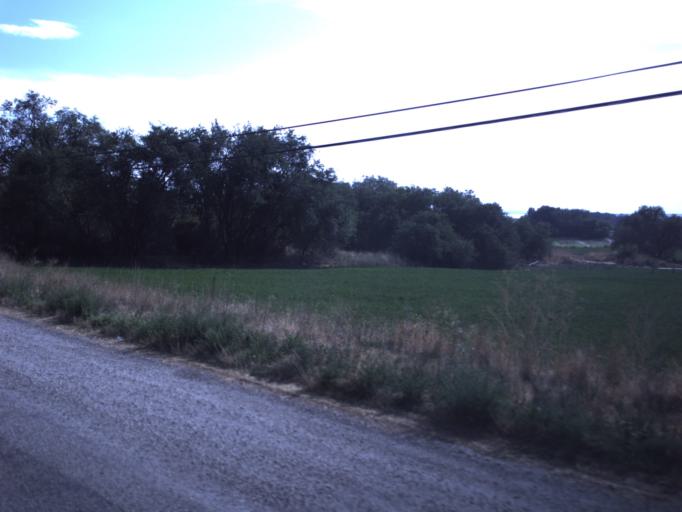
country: US
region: Utah
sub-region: Box Elder County
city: Perry
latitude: 41.4434
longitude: -112.0372
